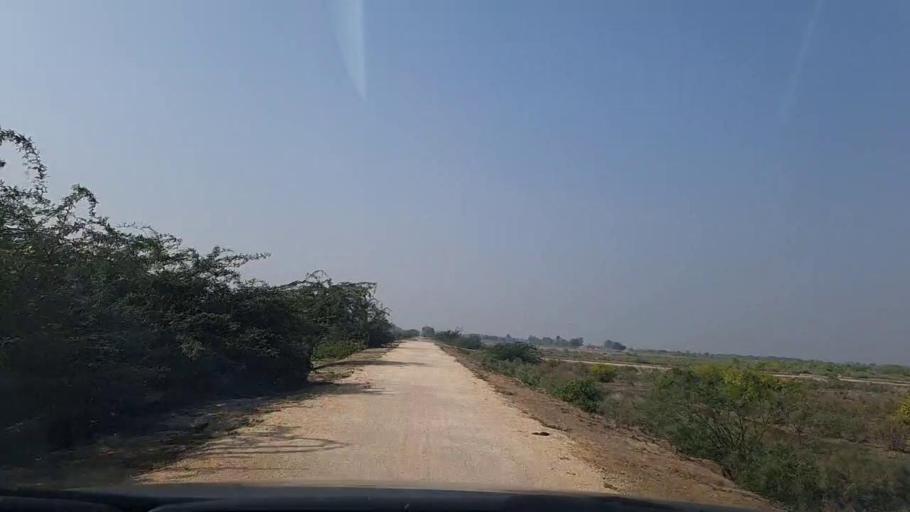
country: PK
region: Sindh
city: Mirpur Sakro
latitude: 24.5752
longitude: 67.7583
